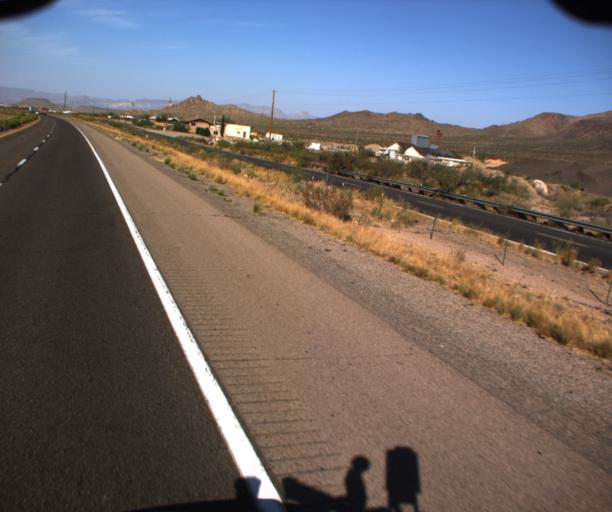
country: US
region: Arizona
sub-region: Mohave County
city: Kingman
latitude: 35.1590
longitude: -114.0813
